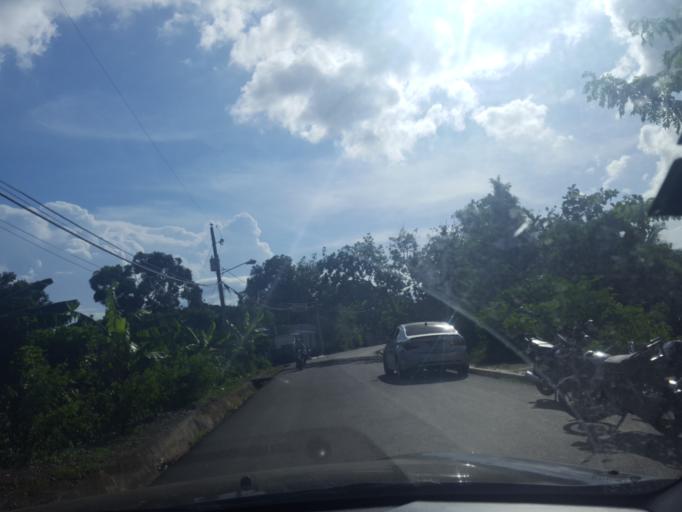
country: DO
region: Santiago
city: Licey al Medio
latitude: 19.3719
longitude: -70.6261
